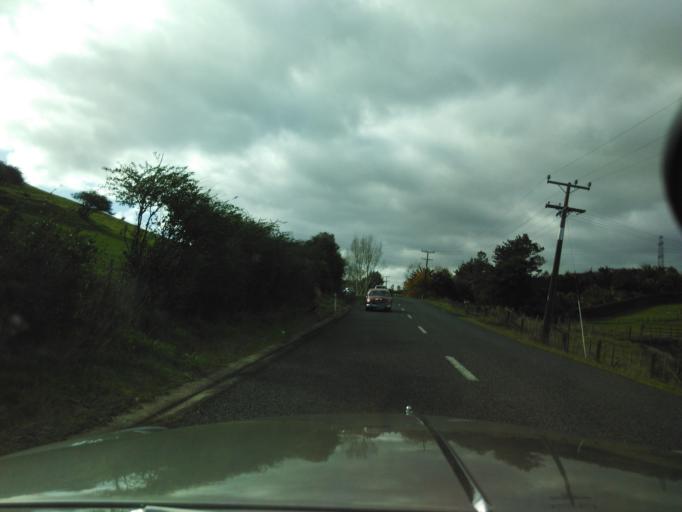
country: NZ
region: Auckland
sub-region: Auckland
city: Red Hill
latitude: -37.0758
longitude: 175.0719
